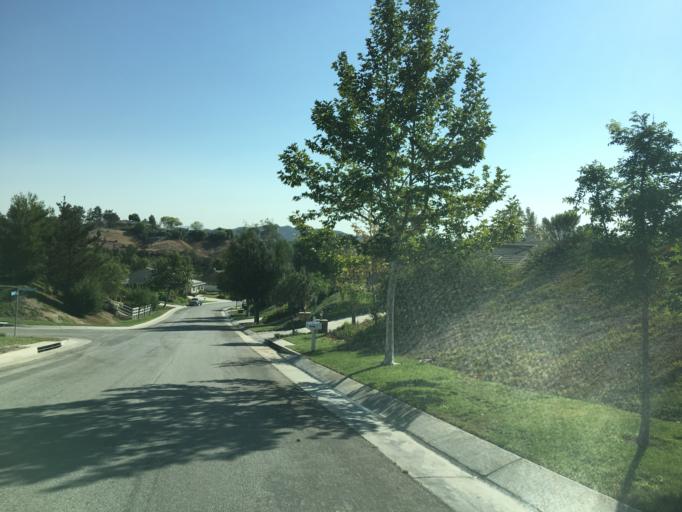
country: US
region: California
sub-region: Los Angeles County
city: Val Verde
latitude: 34.4653
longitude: -118.6694
